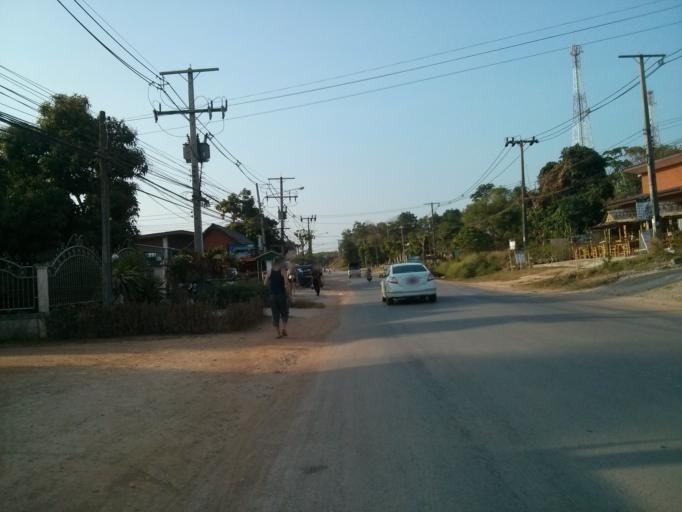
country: TH
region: Krabi
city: Saladan
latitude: 7.5774
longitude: 99.0346
